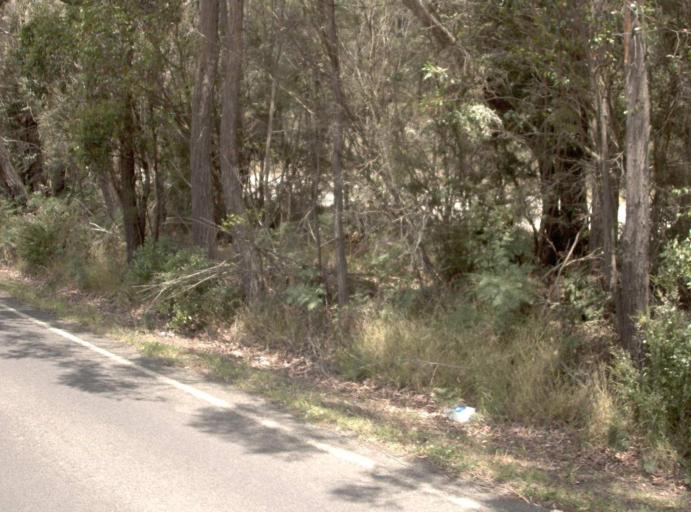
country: AU
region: Victoria
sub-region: Latrobe
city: Traralgon
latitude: -38.2582
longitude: 146.6782
